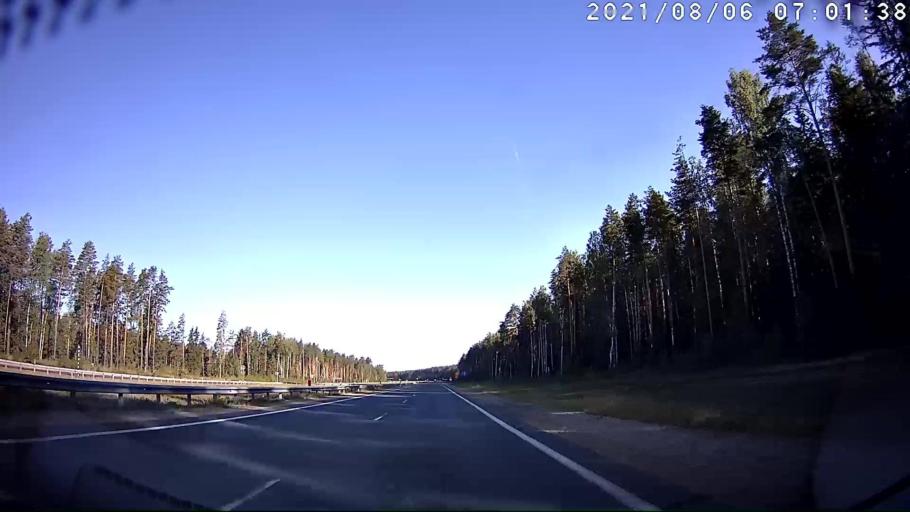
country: RU
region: Mariy-El
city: Surok
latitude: 56.5252
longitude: 48.0076
